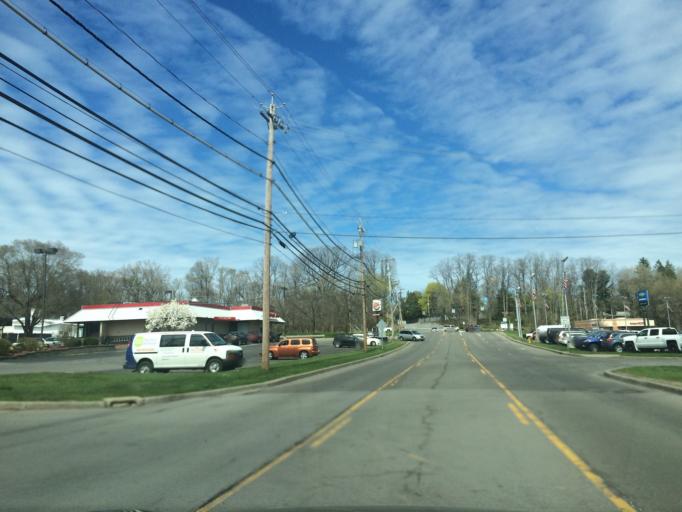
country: US
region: New York
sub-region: Monroe County
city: East Rochester
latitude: 43.1013
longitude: -77.4818
